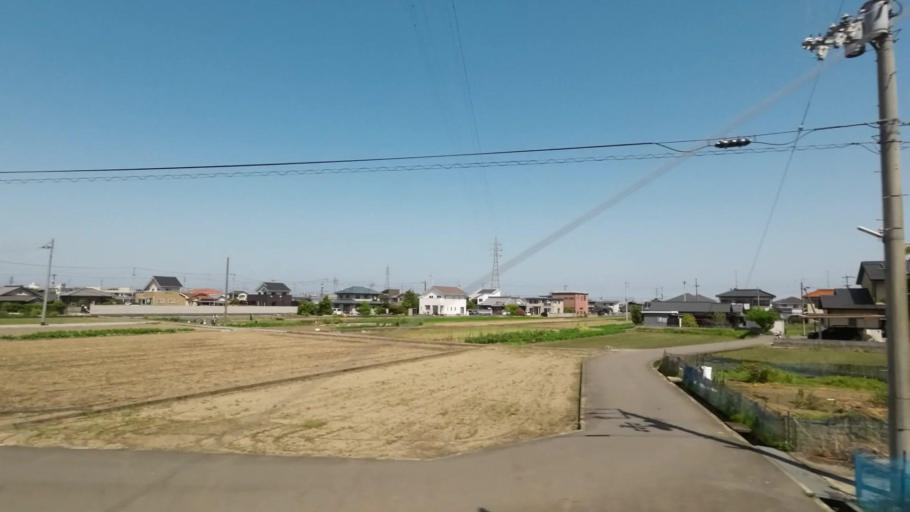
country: JP
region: Ehime
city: Niihama
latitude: 33.9589
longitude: 133.3069
